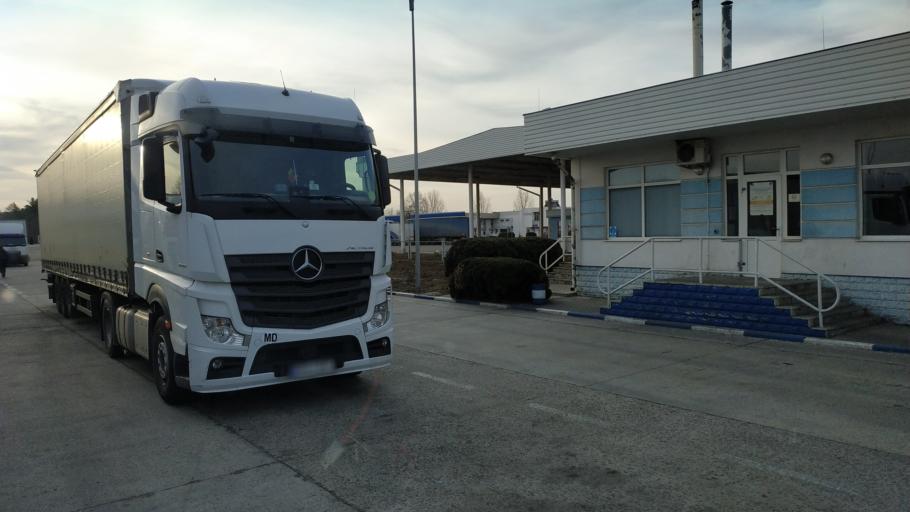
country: RO
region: Vaslui
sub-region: Comuna Dranceni
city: Rasesti
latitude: 46.7937
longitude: 28.1644
